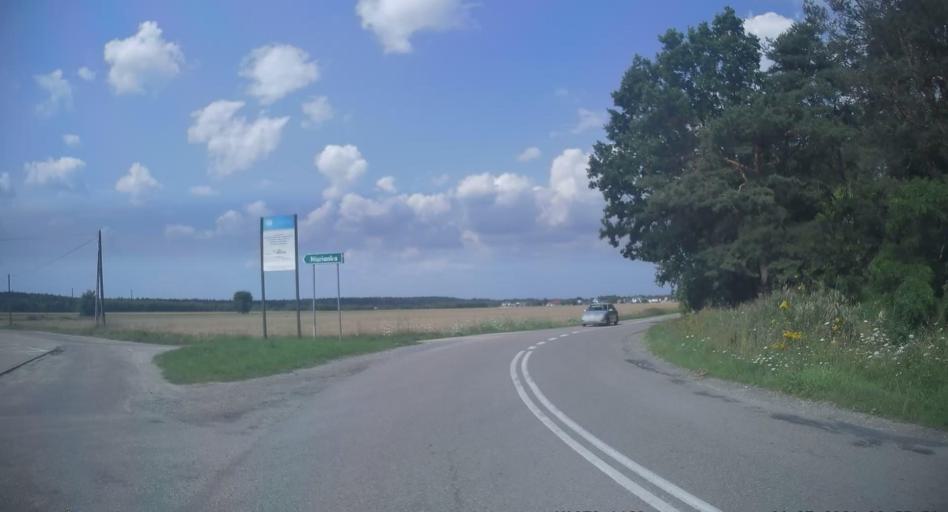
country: PL
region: Lodz Voivodeship
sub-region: Powiat tomaszowski
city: Lubochnia
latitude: 51.5737
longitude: 20.0819
